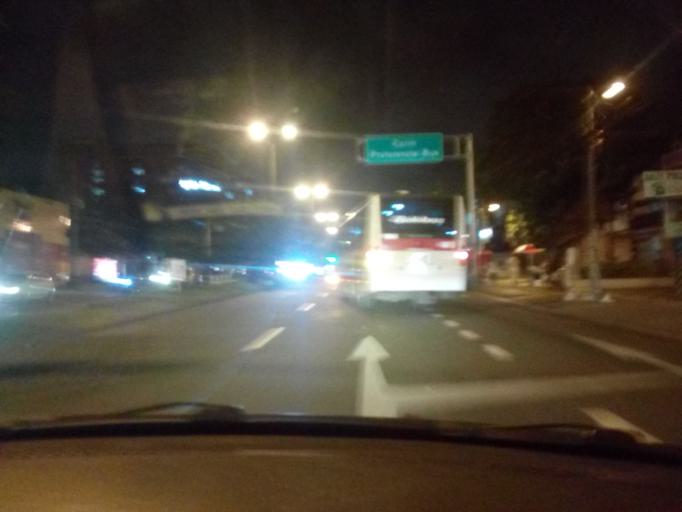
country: CO
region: Antioquia
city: Itagui
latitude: 6.2005
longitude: -75.5888
